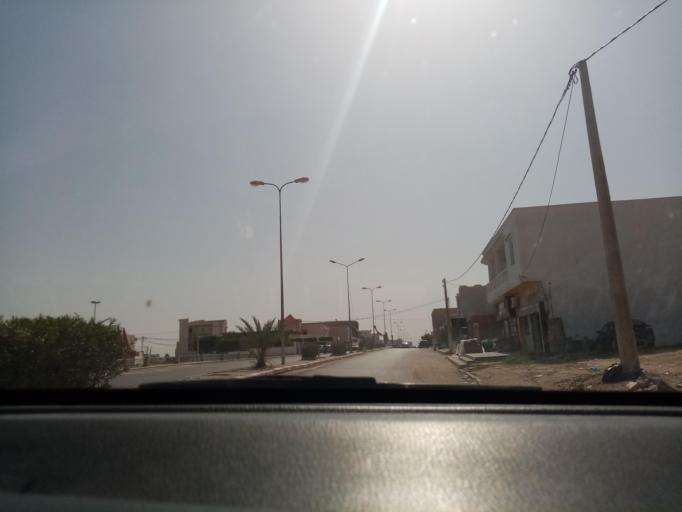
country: TN
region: Qabis
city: Gabes
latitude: 33.8491
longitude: 10.1120
